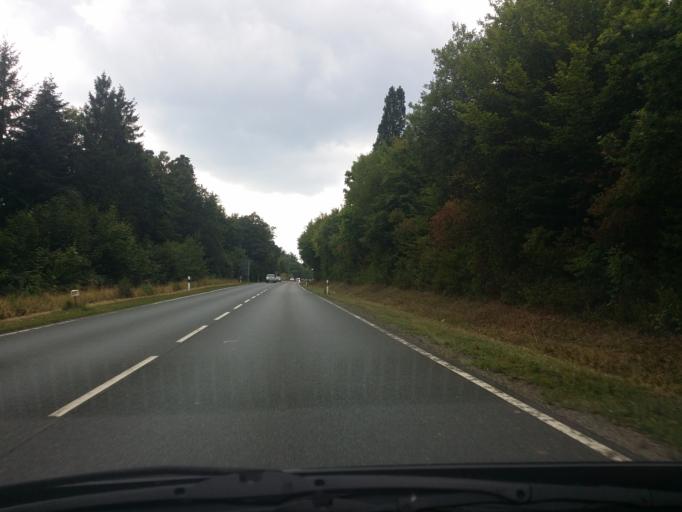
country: DE
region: Hesse
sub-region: Regierungsbezirk Darmstadt
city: Kronberg
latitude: 50.1925
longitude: 8.5121
